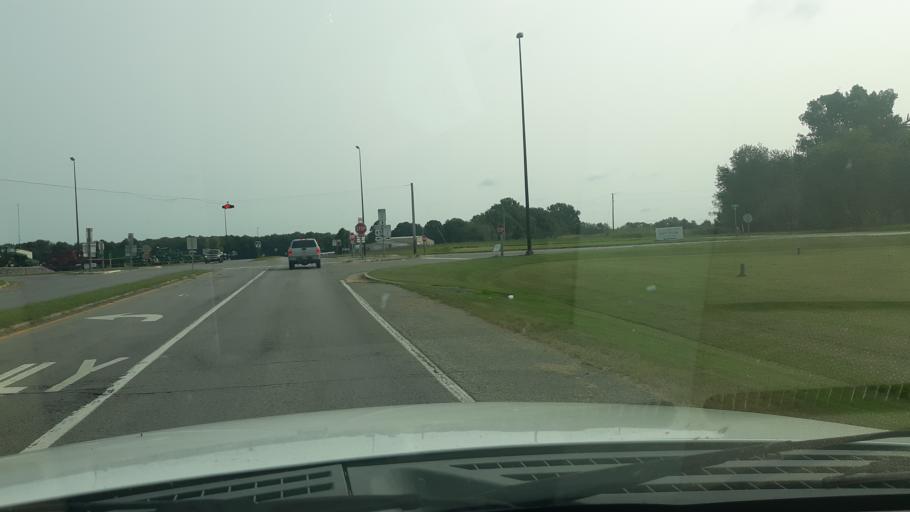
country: US
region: Illinois
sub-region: White County
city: Norris City
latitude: 37.9651
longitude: -88.3289
